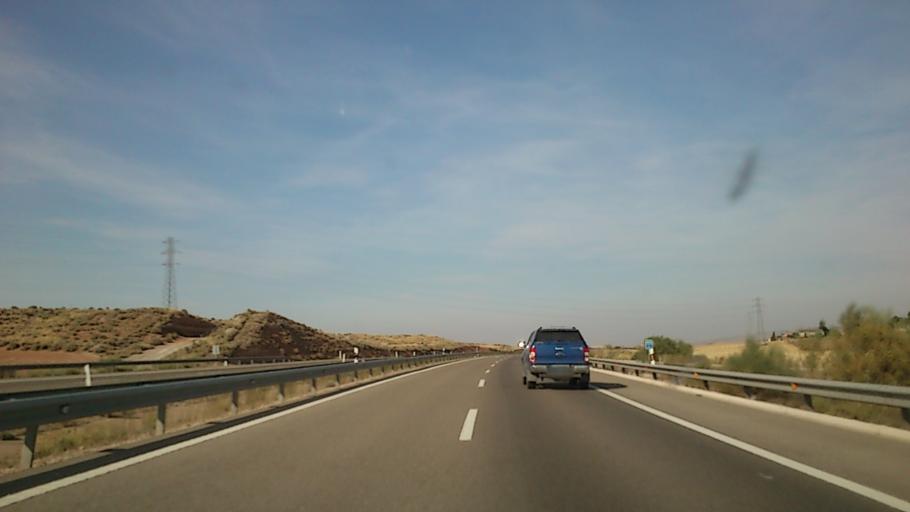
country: ES
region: Aragon
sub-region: Provincia de Zaragoza
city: Longares
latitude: 41.4460
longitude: -1.1382
